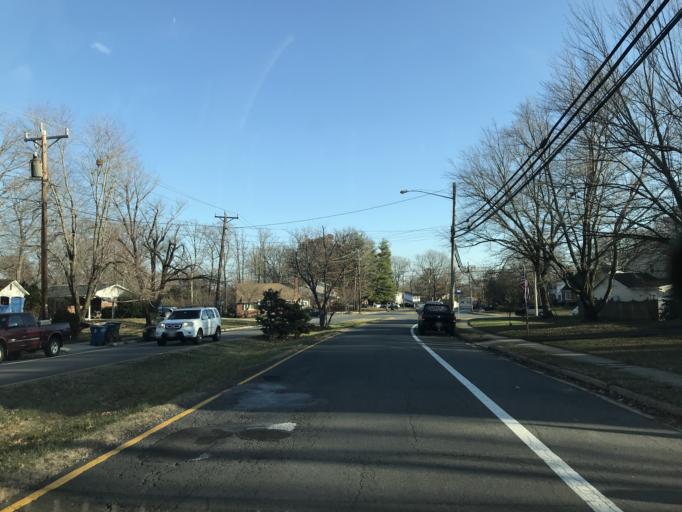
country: US
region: Virginia
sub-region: Fairfax County
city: West Springfield
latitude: 38.7670
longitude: -77.2242
